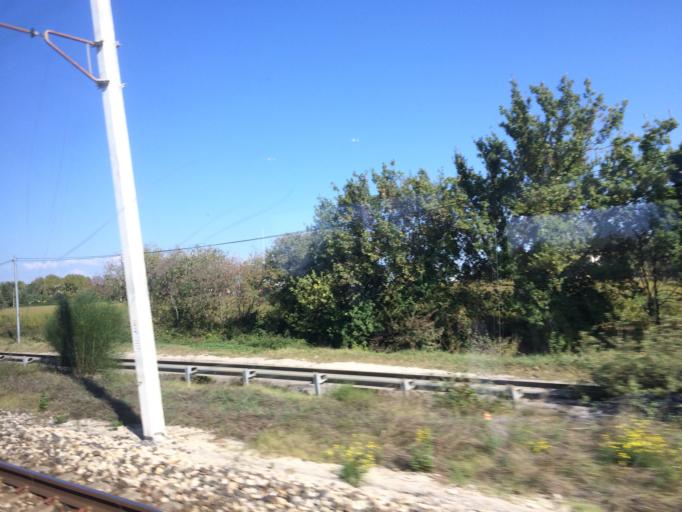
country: FR
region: Provence-Alpes-Cote d'Azur
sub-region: Departement du Vaucluse
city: Le Pontet
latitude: 43.9756
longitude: 4.8632
